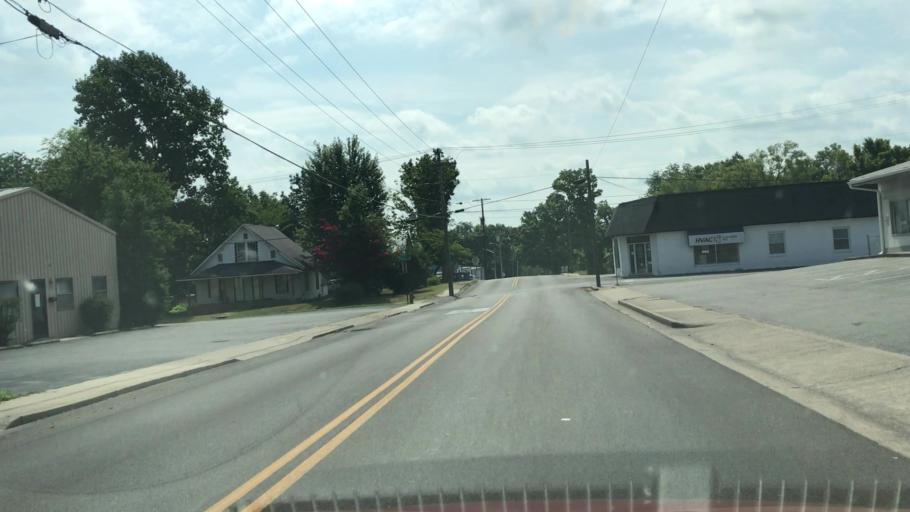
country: US
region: Kentucky
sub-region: Barren County
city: Glasgow
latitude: 36.9922
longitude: -85.9109
